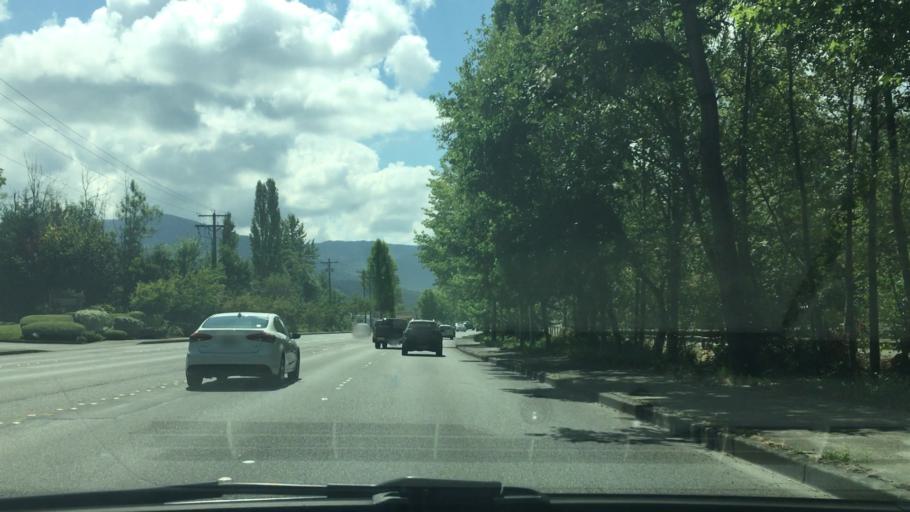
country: US
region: Washington
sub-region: King County
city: Issaquah
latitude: 47.5561
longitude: -122.0459
